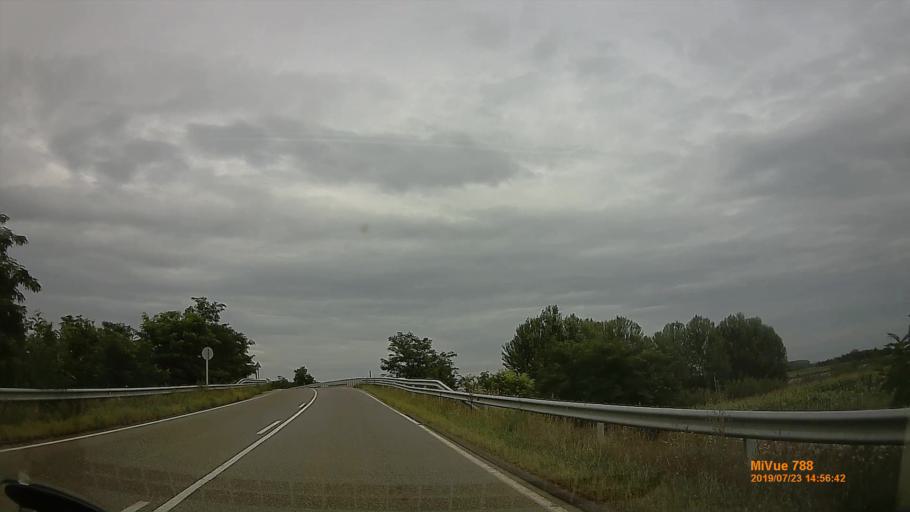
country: HU
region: Szabolcs-Szatmar-Bereg
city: Nyiregyhaza
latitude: 47.9006
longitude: 21.6665
